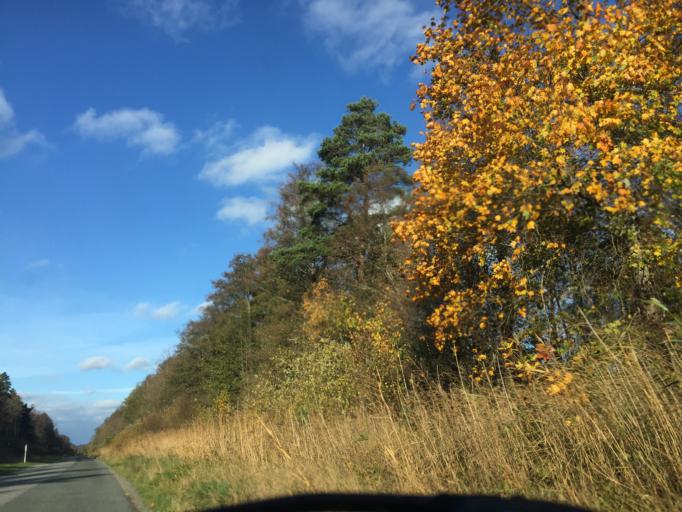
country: LV
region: Liepaja
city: Vec-Liepaja
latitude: 56.5722
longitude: 21.0491
